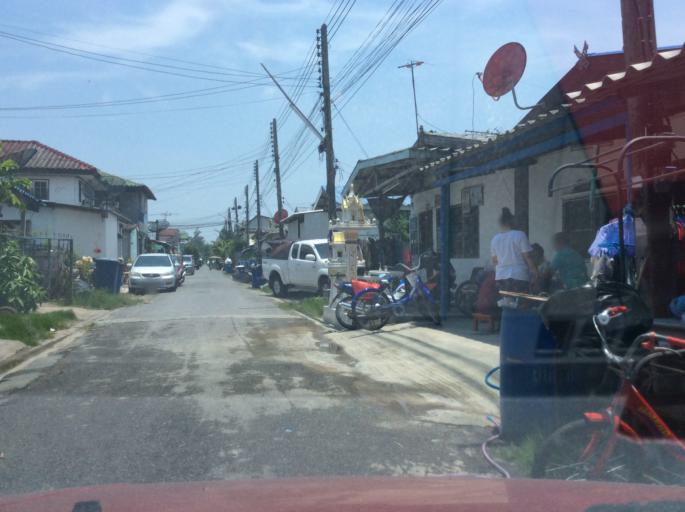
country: TH
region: Pathum Thani
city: Lam Luk Ka
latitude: 13.9485
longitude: 100.7365
